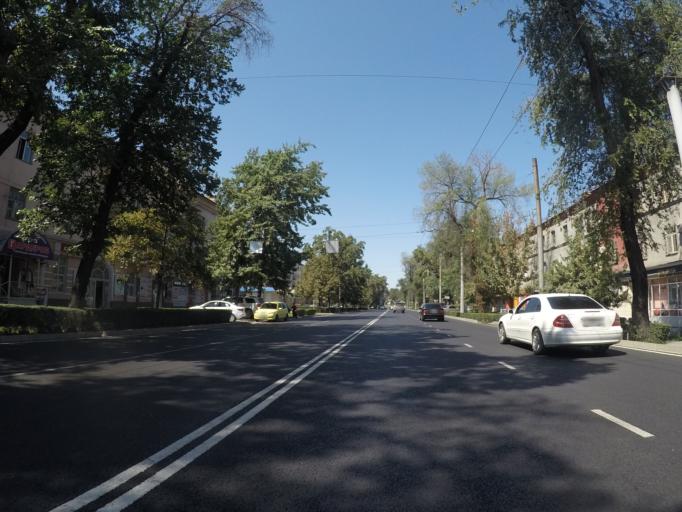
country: KG
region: Chuy
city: Bishkek
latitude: 42.8767
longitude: 74.5846
